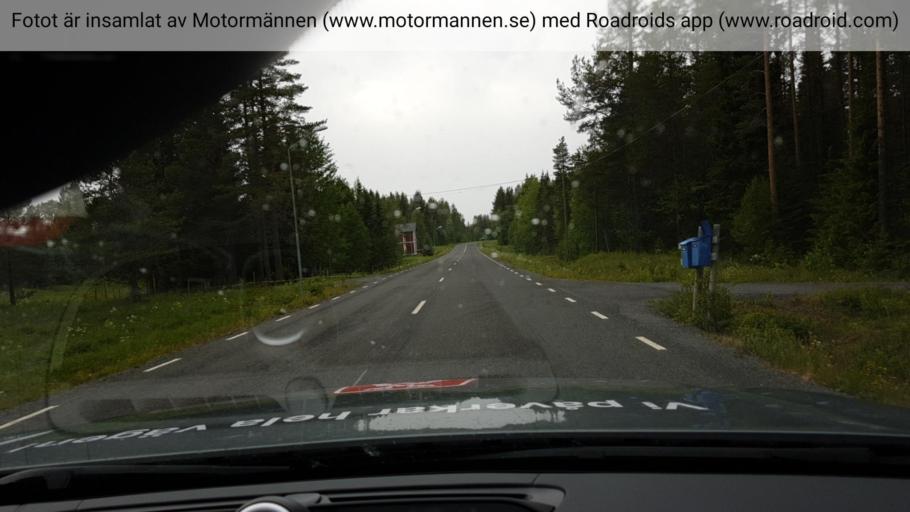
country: SE
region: Jaemtland
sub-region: Stroemsunds Kommun
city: Stroemsund
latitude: 63.6308
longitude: 15.2122
